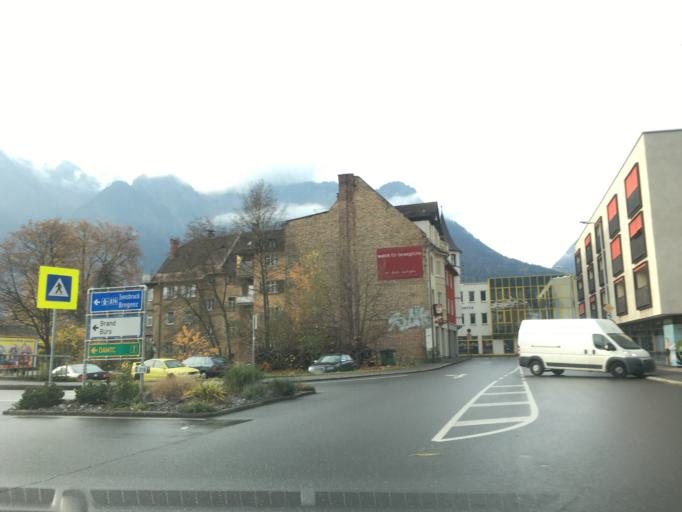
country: AT
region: Vorarlberg
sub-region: Politischer Bezirk Bludenz
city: Bludenz
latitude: 47.1549
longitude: 9.8171
